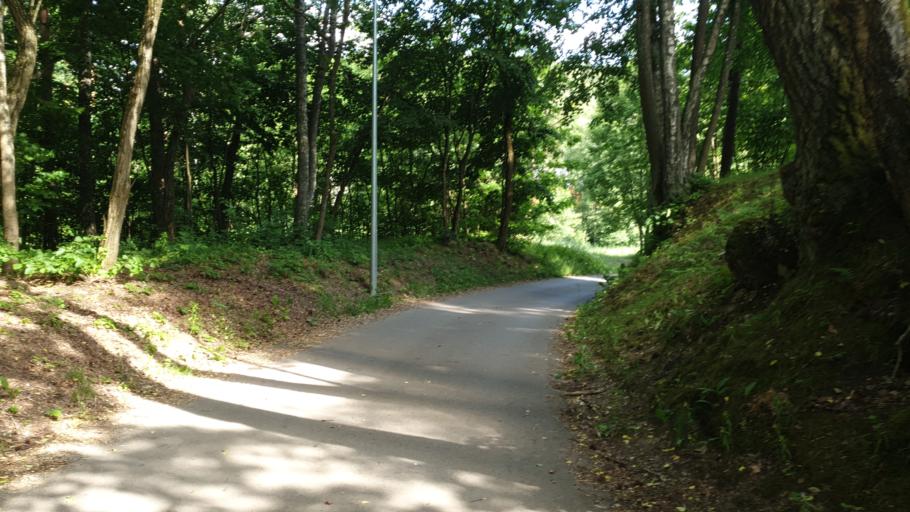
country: LT
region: Vilnius County
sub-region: Vilnius
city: Fabijoniskes
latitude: 54.7851
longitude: 25.3254
